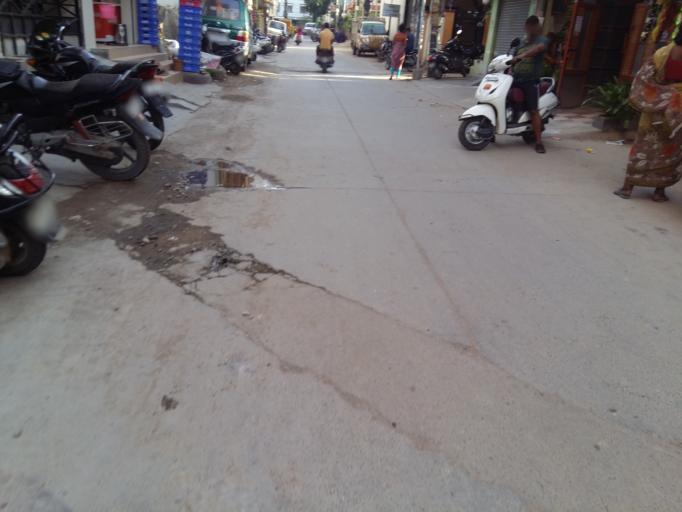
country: IN
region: Telangana
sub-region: Rangareddi
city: Kukatpalli
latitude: 17.4874
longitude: 78.3982
